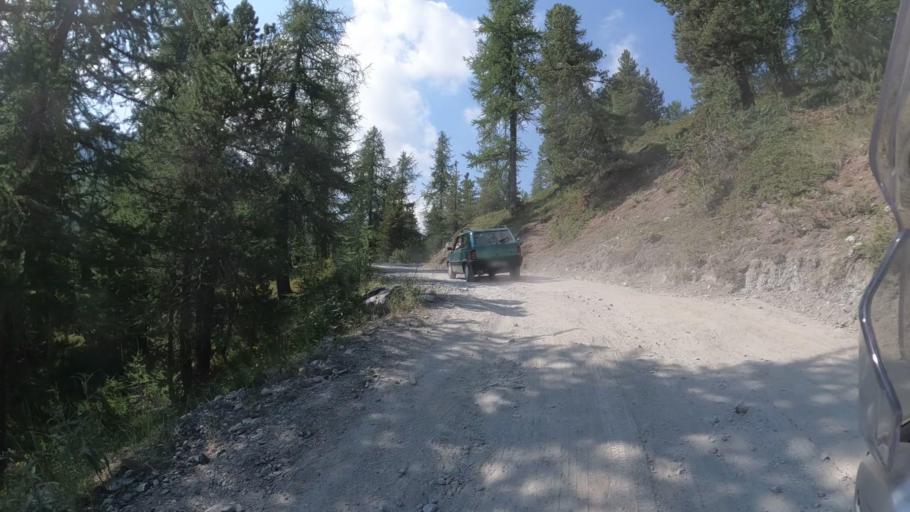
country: IT
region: Piedmont
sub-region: Provincia di Torino
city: Cesana Torinese
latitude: 44.9154
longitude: 6.8017
